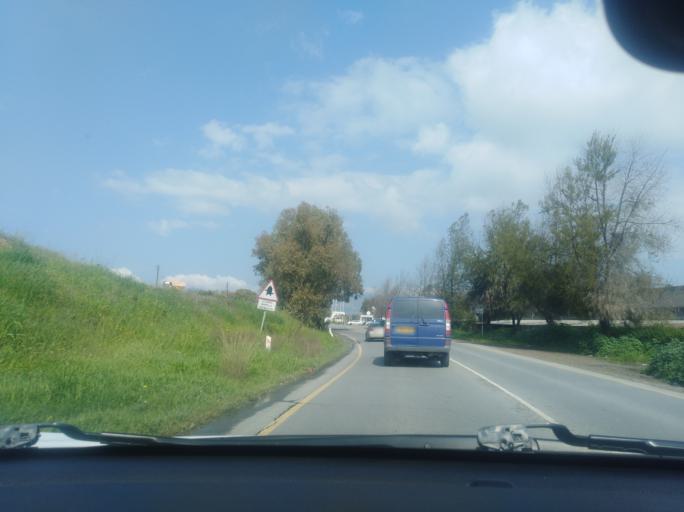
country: CY
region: Lefkosia
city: Nicosia
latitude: 35.1628
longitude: 33.3990
